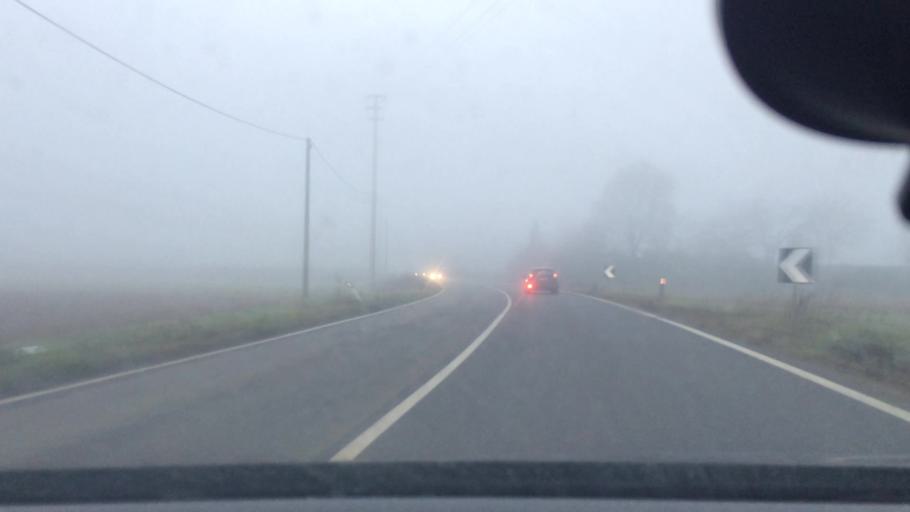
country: IT
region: Lombardy
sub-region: Citta metropolitana di Milano
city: Cantalupo
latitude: 45.5697
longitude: 8.9956
